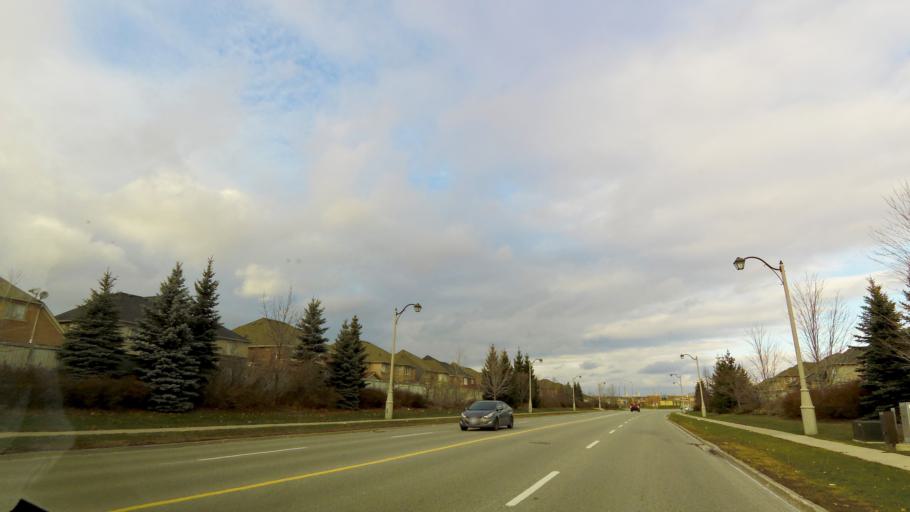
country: CA
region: Ontario
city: Brampton
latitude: 43.7710
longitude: -79.7056
